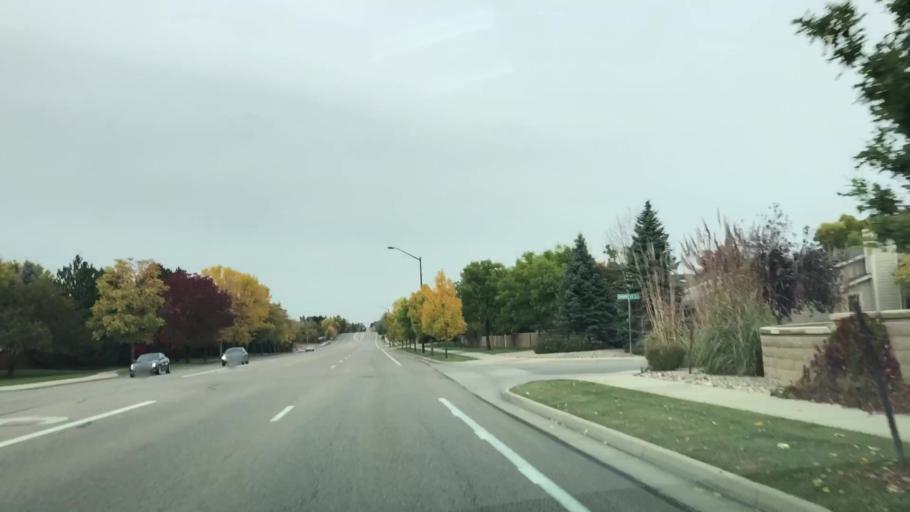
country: US
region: Colorado
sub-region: Larimer County
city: Fort Collins
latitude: 40.4958
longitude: -105.0581
